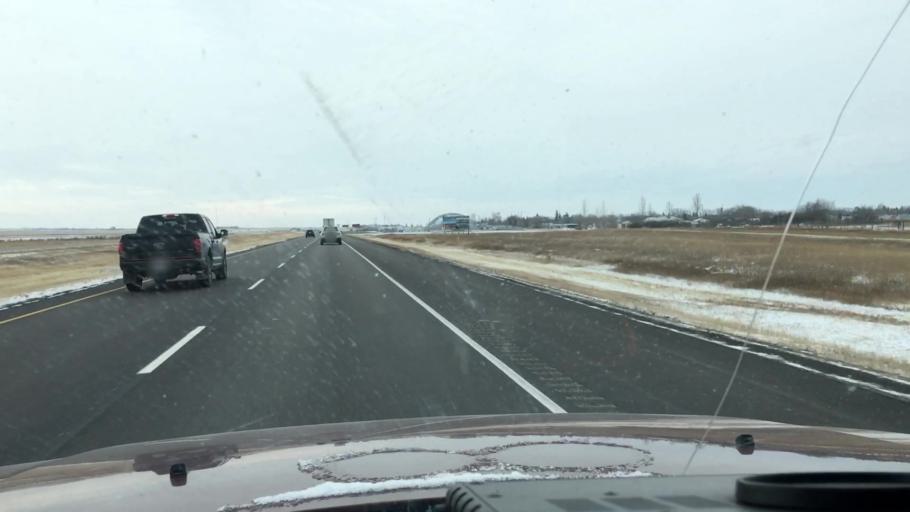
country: CA
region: Saskatchewan
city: Saskatoon
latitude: 51.8209
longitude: -106.4995
